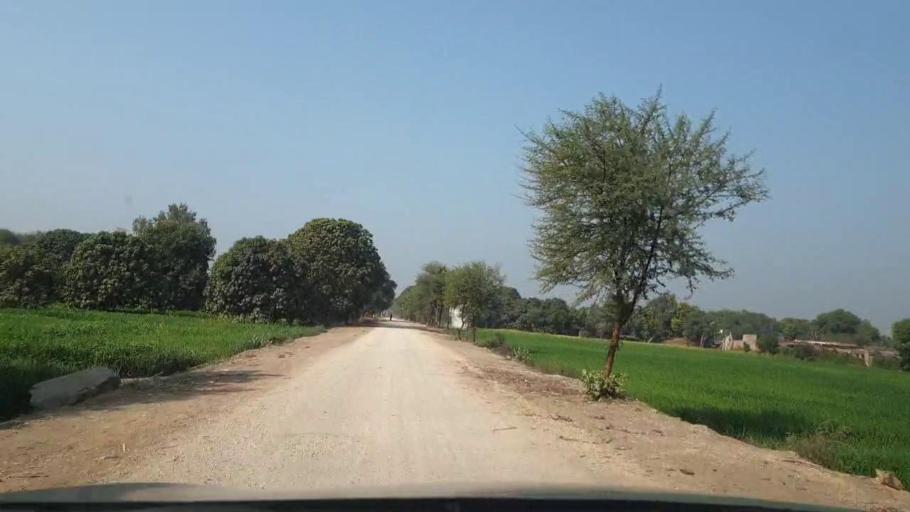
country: PK
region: Sindh
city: Tando Allahyar
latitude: 25.5180
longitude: 68.7557
